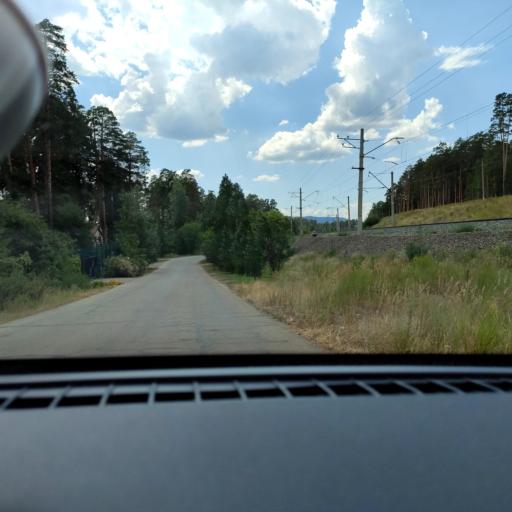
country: RU
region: Samara
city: Volzhskiy
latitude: 53.4332
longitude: 50.1456
